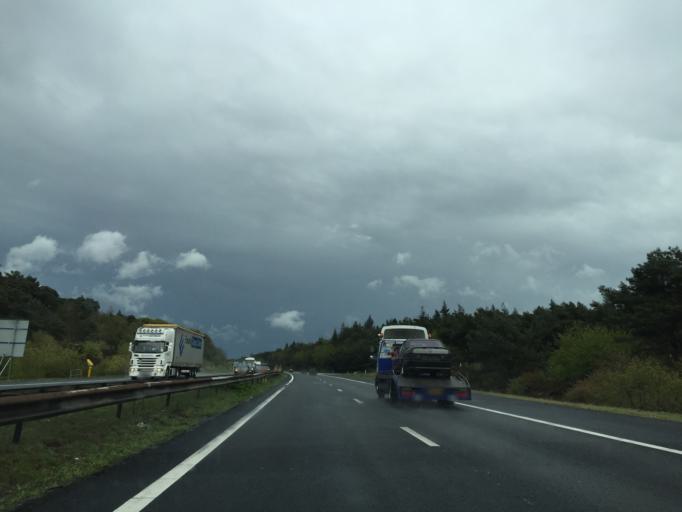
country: NL
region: Gelderland
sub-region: Gemeente Nunspeet
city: Nunspeet
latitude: 52.3620
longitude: 5.7861
